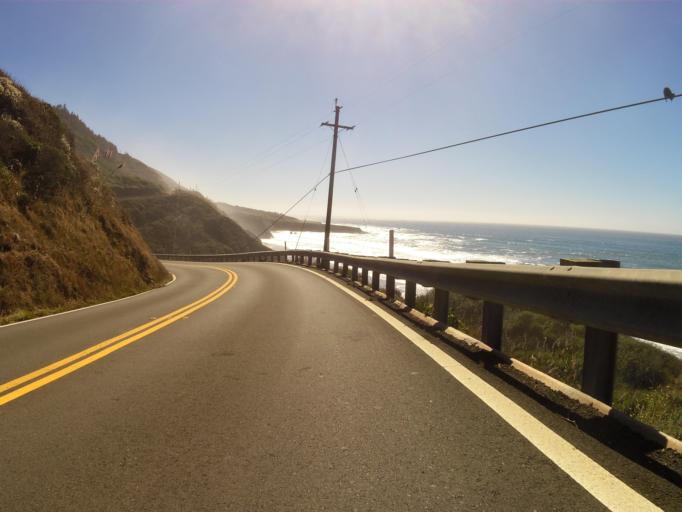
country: US
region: California
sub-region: Mendocino County
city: Fort Bragg
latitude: 39.6150
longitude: -123.7818
